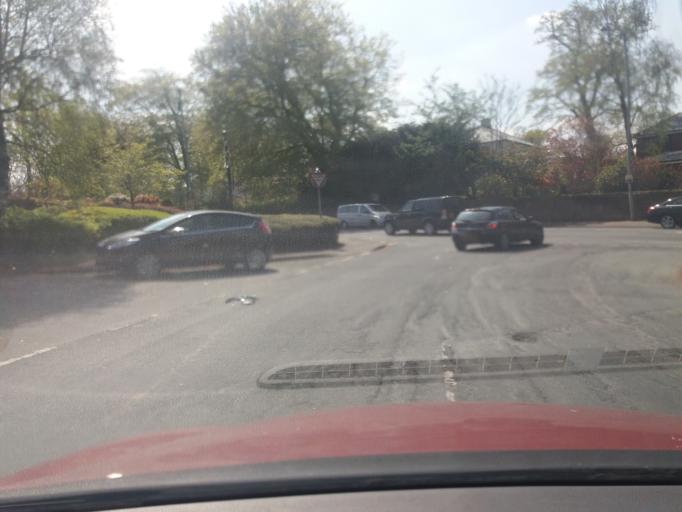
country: GB
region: England
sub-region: Lancashire
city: Clayton-le-Woods
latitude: 53.6833
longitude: -2.6383
